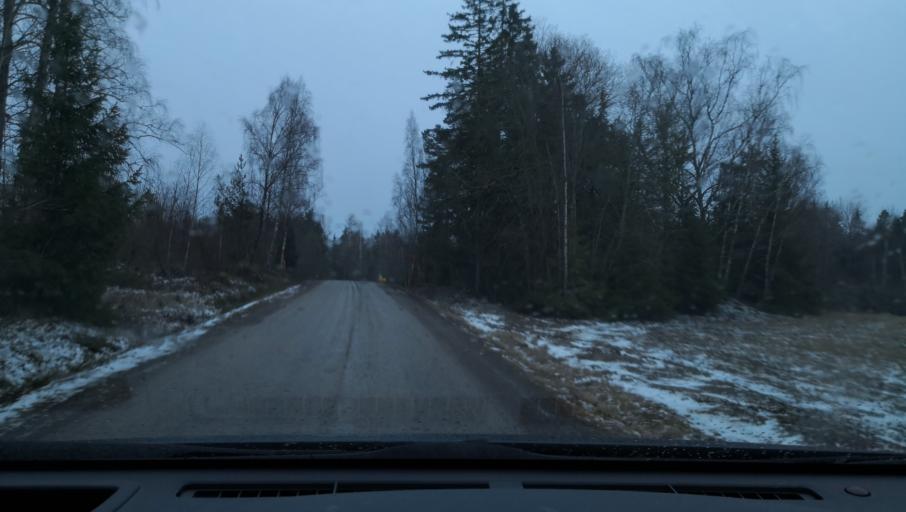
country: SE
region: Uppsala
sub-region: Enkopings Kommun
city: Hummelsta
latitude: 59.4613
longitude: 16.8258
